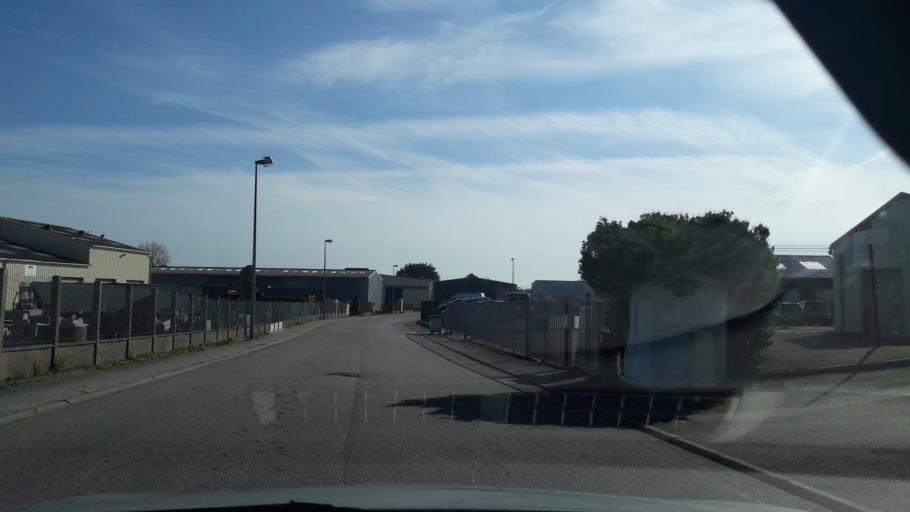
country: FR
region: Lower Normandy
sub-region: Departement de la Manche
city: Querqueville
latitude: 49.6593
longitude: -1.6853
